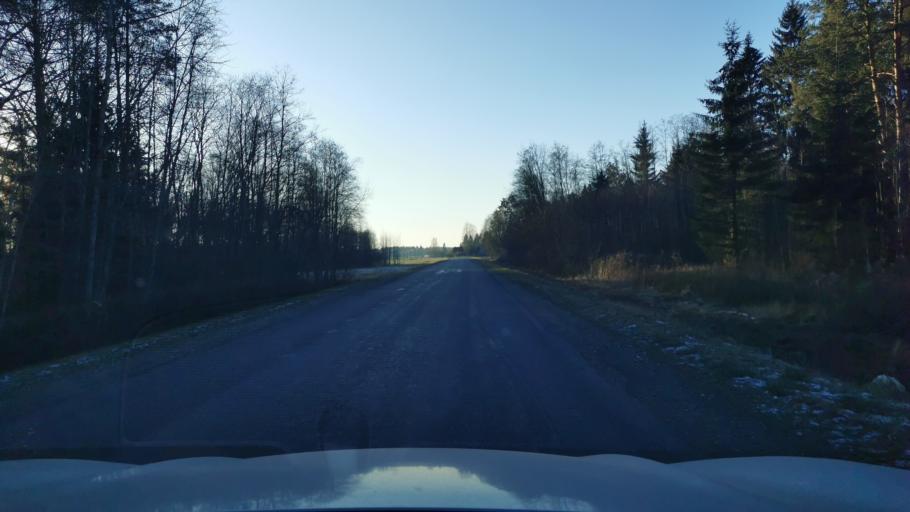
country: EE
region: Ida-Virumaa
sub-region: Kivioli linn
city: Kivioli
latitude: 59.3124
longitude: 27.0024
